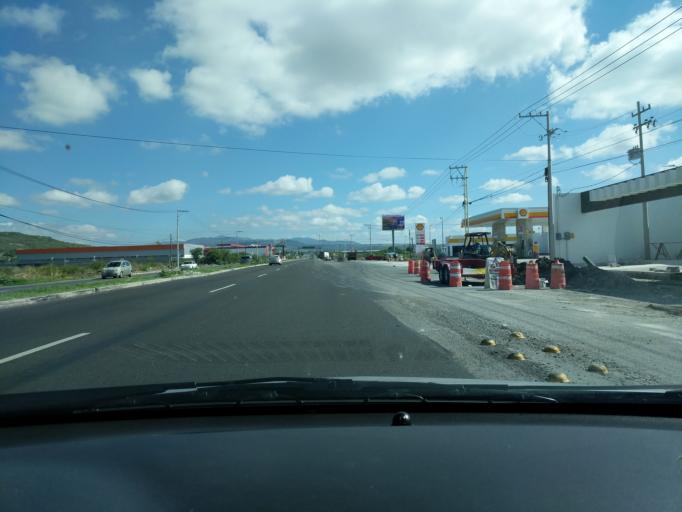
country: MX
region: Queretaro
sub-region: Queretaro
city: Patria Nueva
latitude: 20.6363
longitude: -100.4998
